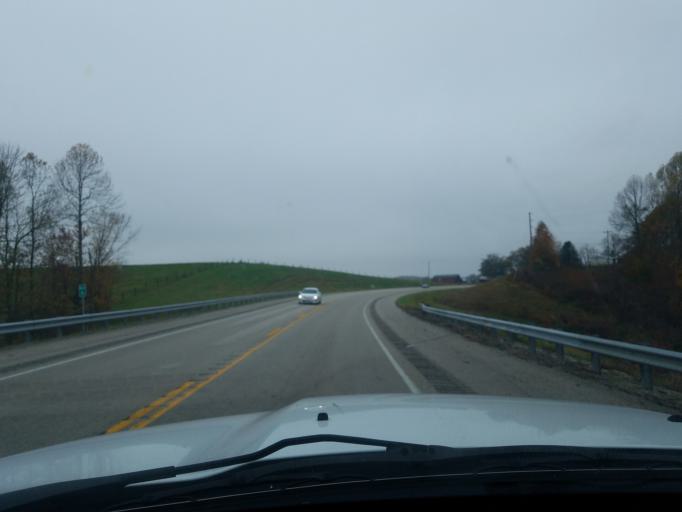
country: US
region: Kentucky
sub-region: Green County
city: Greensburg
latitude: 37.4181
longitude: -85.5112
